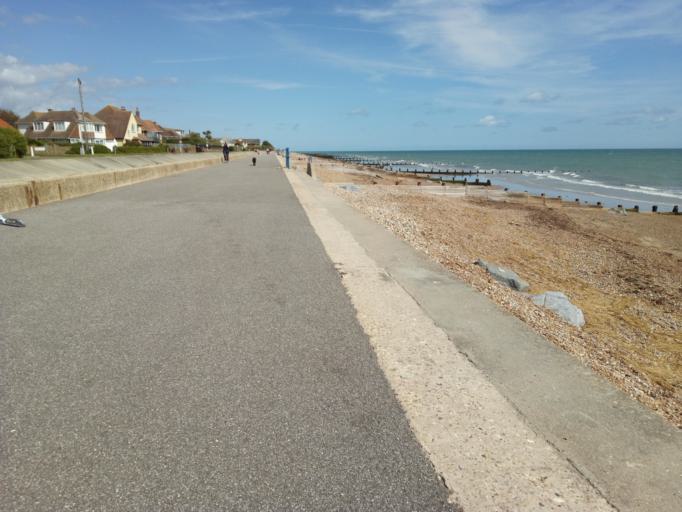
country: GB
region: England
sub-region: West Sussex
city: Bognor Regis
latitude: 50.7876
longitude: -0.6418
